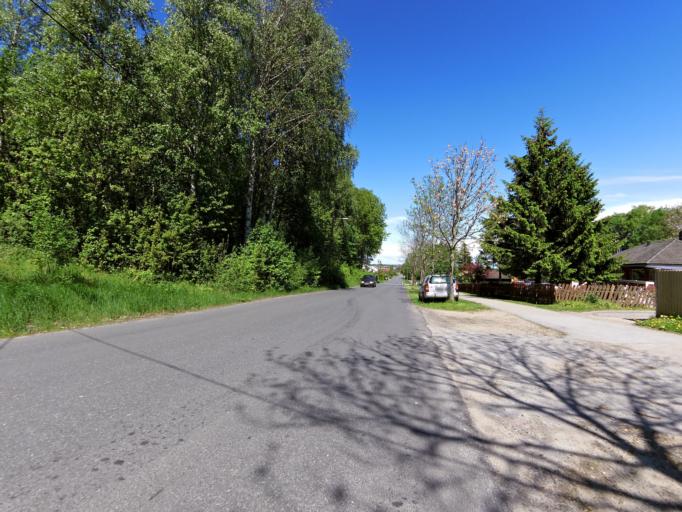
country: NO
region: Ostfold
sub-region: Fredrikstad
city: Fredrikstad
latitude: 59.2264
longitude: 10.9672
